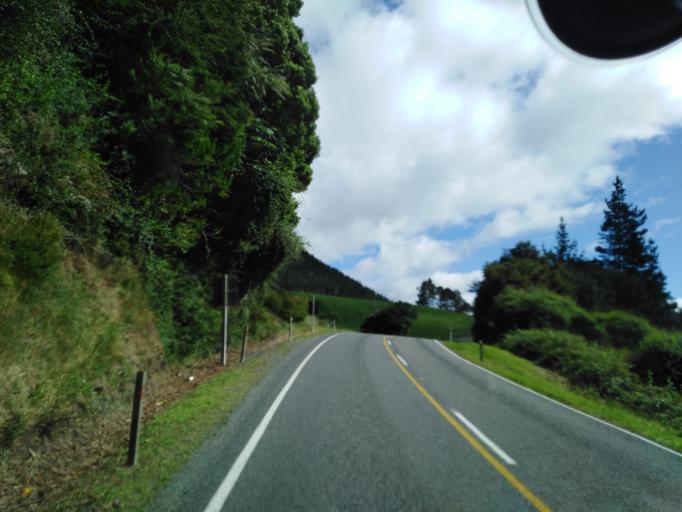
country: NZ
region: Nelson
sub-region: Nelson City
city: Nelson
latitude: -41.2891
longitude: 173.5715
